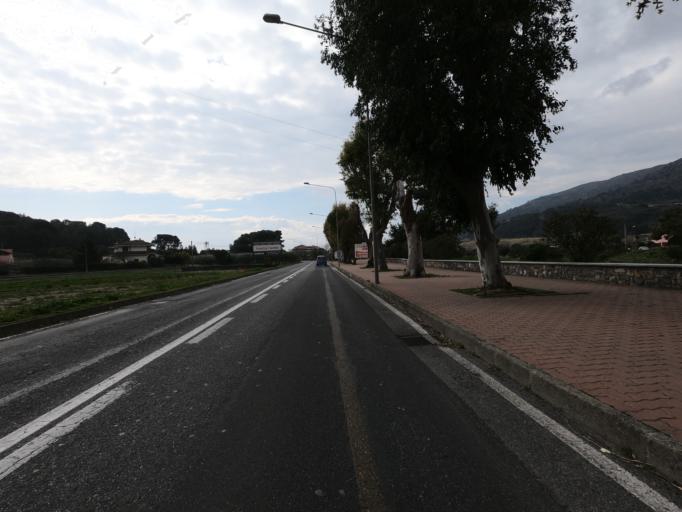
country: IT
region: Liguria
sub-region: Provincia di Savona
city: Andora
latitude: 43.9642
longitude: 8.1418
